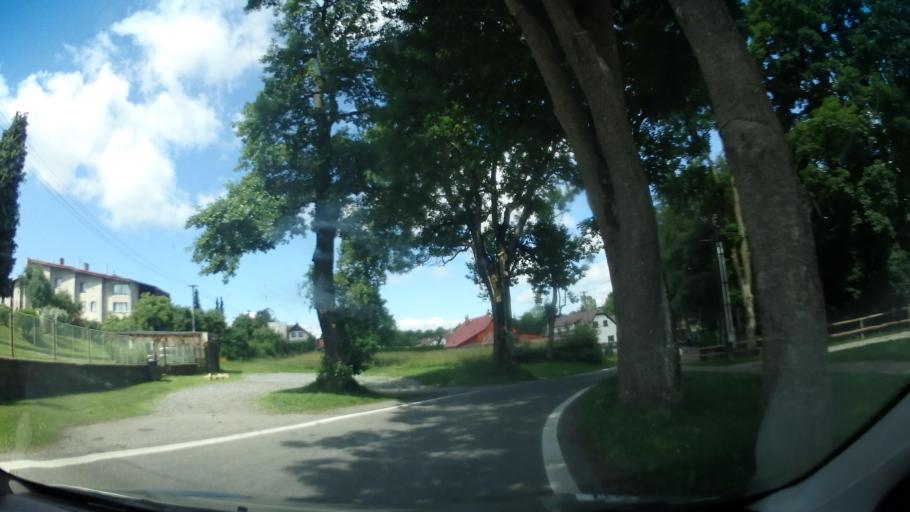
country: CZ
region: Vysocina
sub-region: Okres Zd'ar nad Sazavou
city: Nove Mesto na Morave
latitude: 49.6302
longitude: 16.0452
